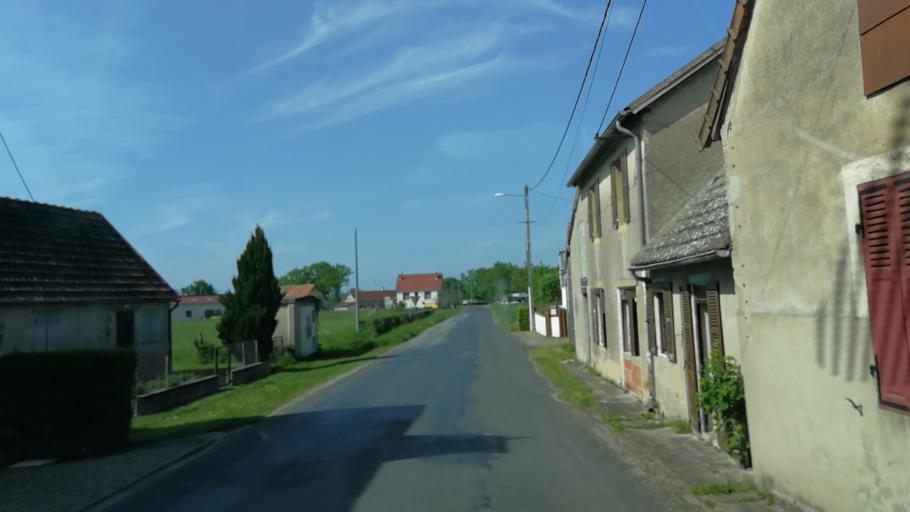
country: FR
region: Auvergne
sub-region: Departement de l'Allier
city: Neuilly-le-Real
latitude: 46.4054
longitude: 3.5757
